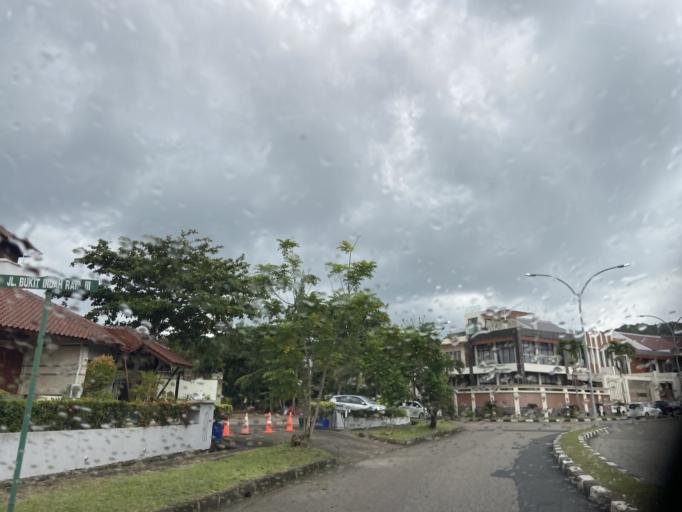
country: SG
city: Singapore
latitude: 1.1042
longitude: 104.0262
